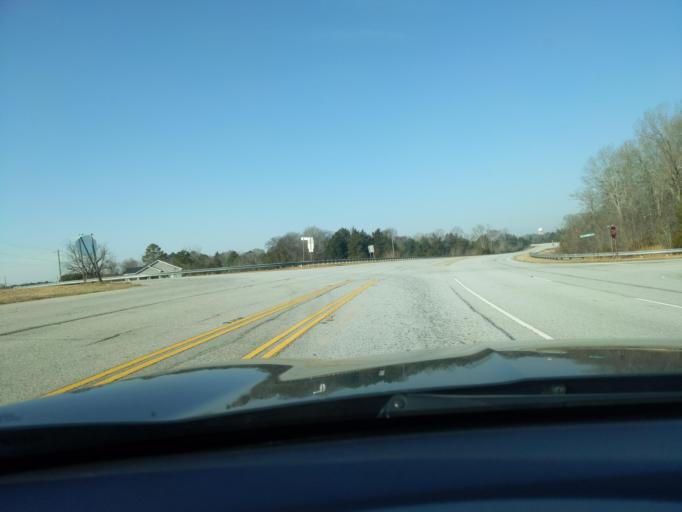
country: US
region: South Carolina
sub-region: Abbeville County
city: Calhoun Falls
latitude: 34.0947
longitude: -82.5707
